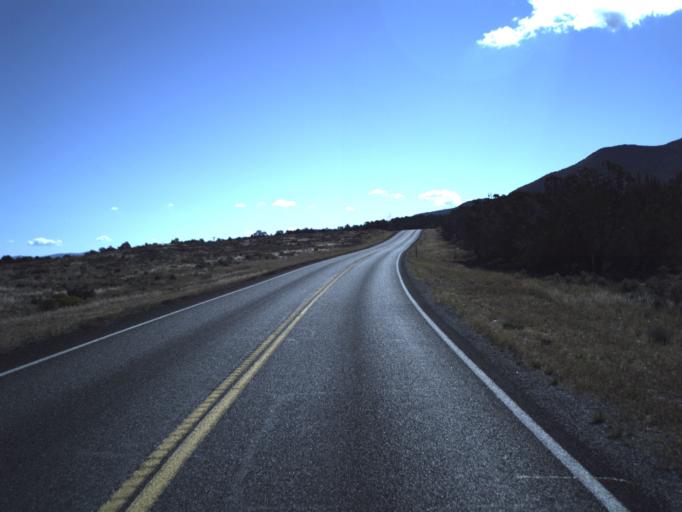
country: US
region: Utah
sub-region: Iron County
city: Cedar City
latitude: 37.6106
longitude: -113.3728
